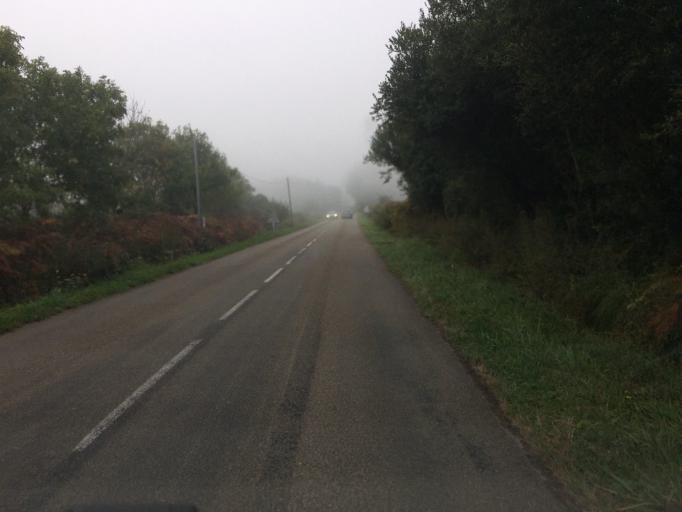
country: FR
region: Brittany
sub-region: Departement du Finistere
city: Plogoff
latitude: 48.0623
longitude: -4.6427
